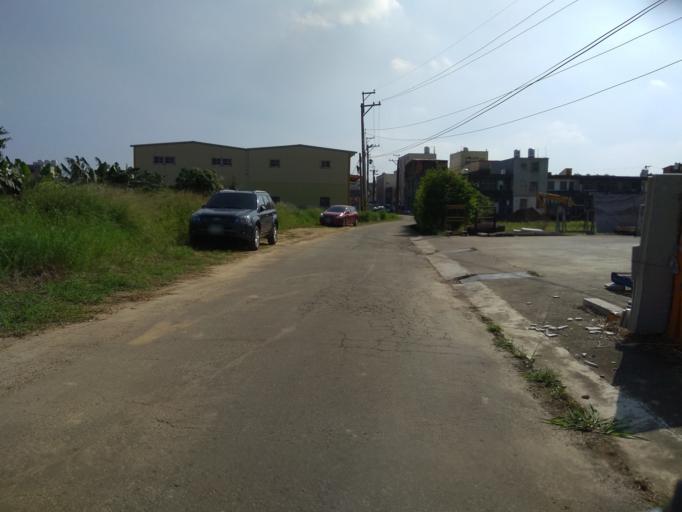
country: TW
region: Taiwan
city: Taoyuan City
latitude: 25.0509
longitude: 121.2218
